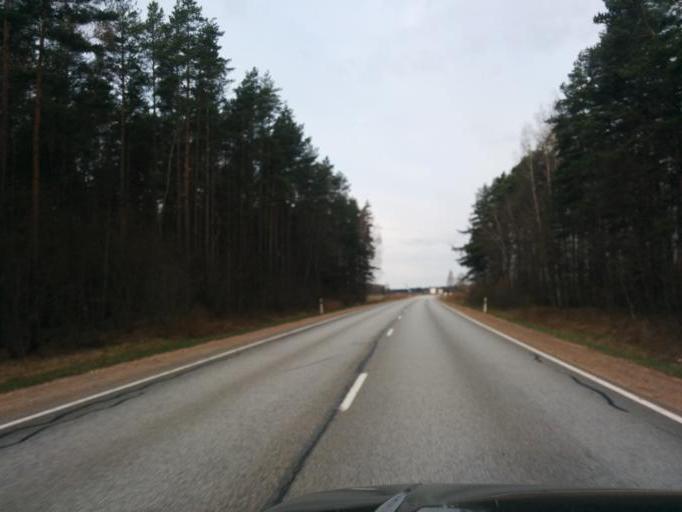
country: LV
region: Kekava
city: Kekava
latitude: 56.8091
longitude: 24.1908
